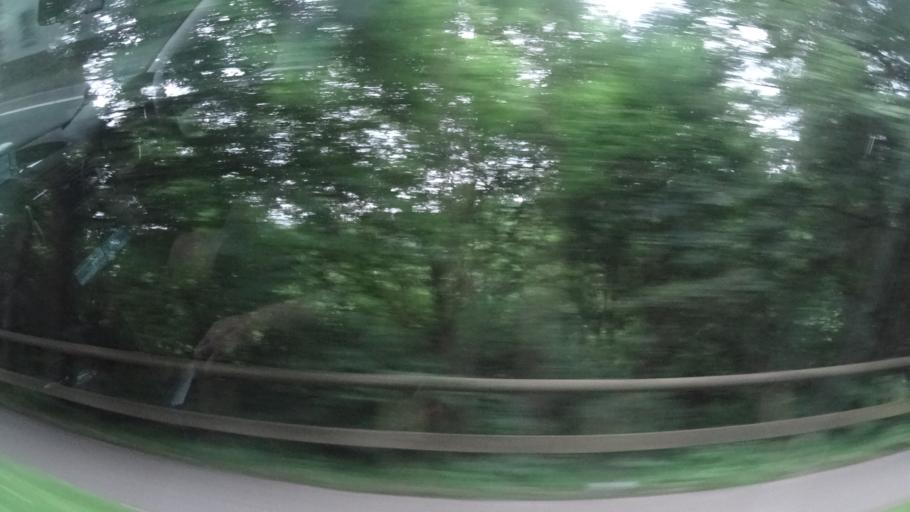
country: DE
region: Lower Saxony
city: Bodenwerder
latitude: 51.9834
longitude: 9.5324
